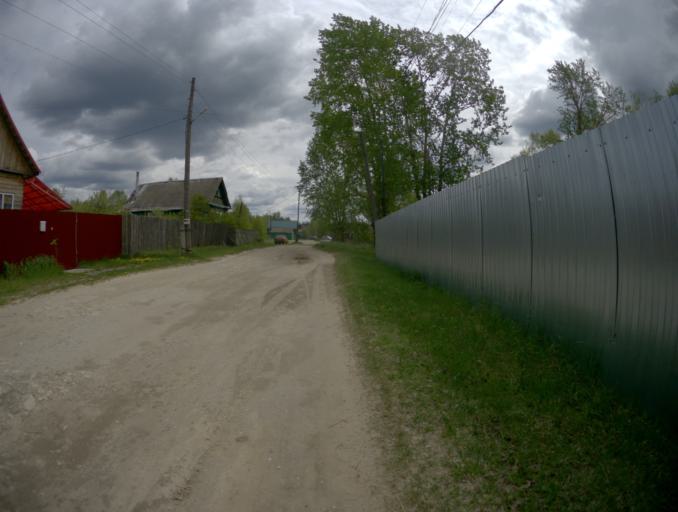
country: RU
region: Vladimir
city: Kurlovo
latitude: 55.4479
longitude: 40.6248
